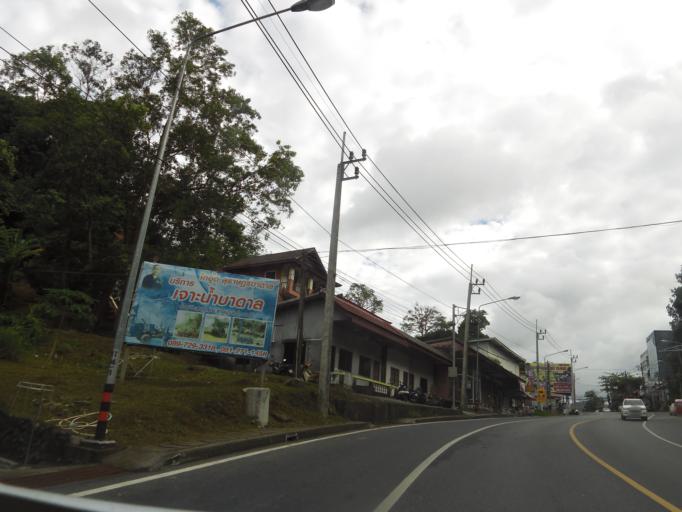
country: TH
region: Phuket
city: Patong
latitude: 7.8720
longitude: 98.2870
